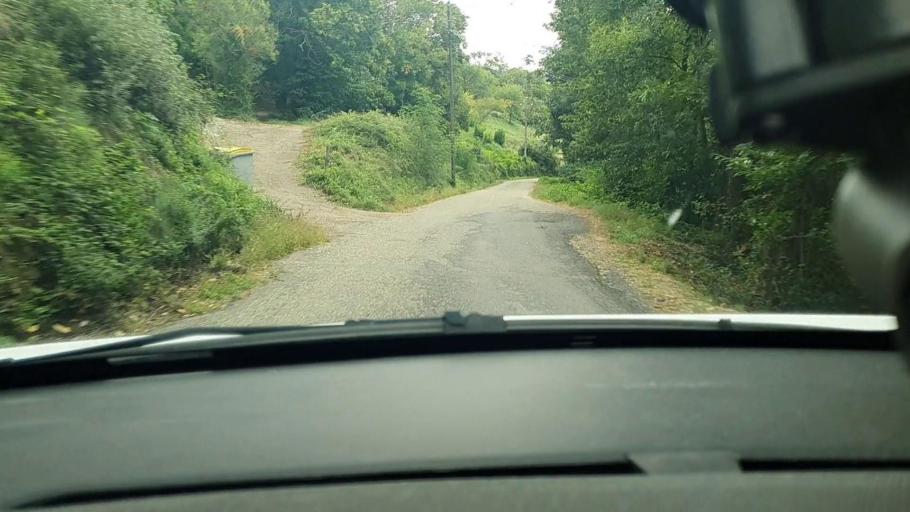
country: FR
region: Languedoc-Roussillon
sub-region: Departement du Gard
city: Branoux-les-Taillades
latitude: 44.2554
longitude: 3.9769
